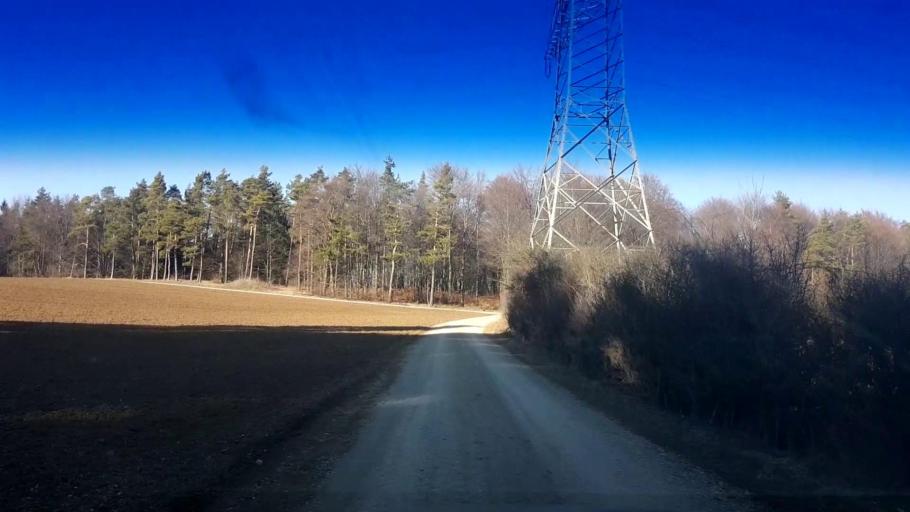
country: DE
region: Bavaria
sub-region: Upper Franconia
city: Poxdorf
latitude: 49.9659
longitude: 11.0857
